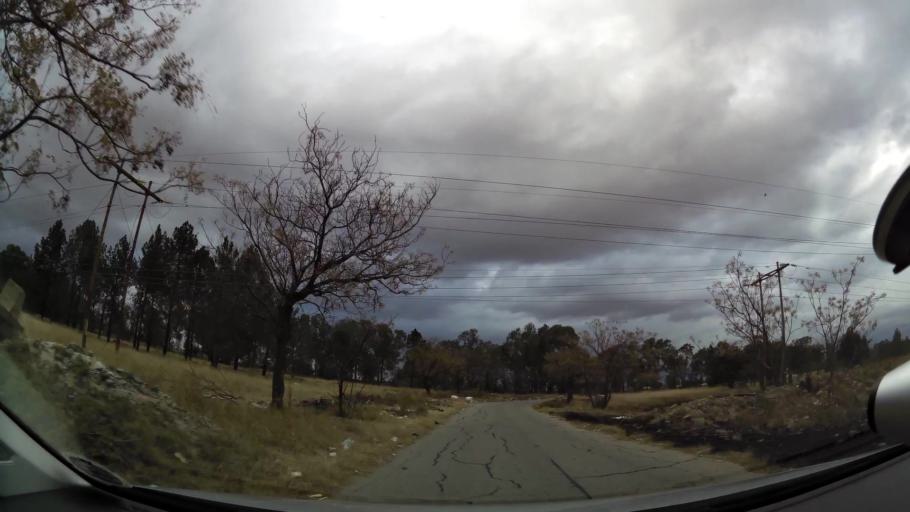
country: ZA
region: Orange Free State
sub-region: Lejweleputswa District Municipality
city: Welkom
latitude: -27.9654
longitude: 26.7031
